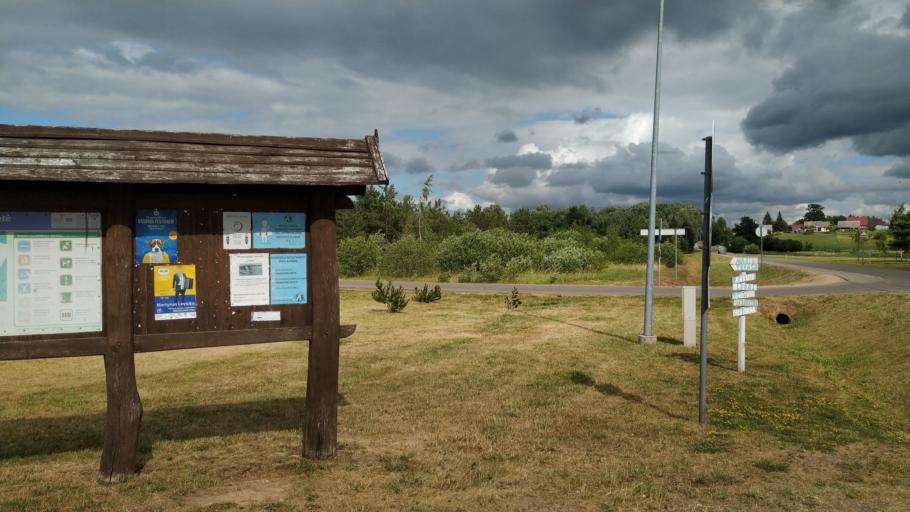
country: LT
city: Kupiskis
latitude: 55.8498
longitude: 24.9764
